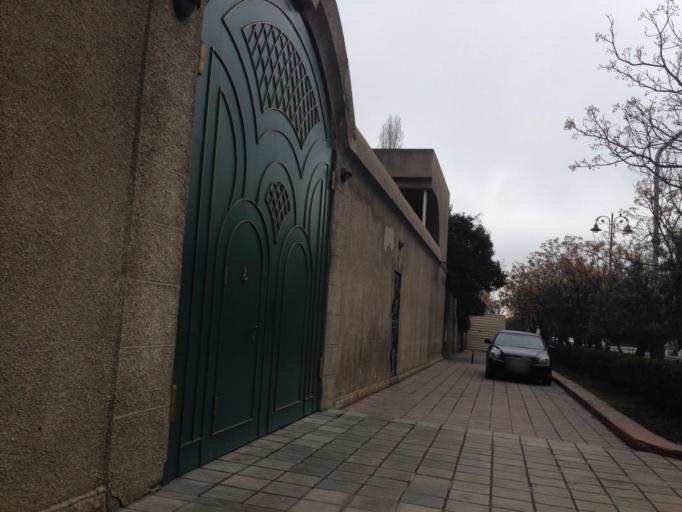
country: AZ
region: Baki
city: Bilajari
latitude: 40.4109
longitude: 49.8480
